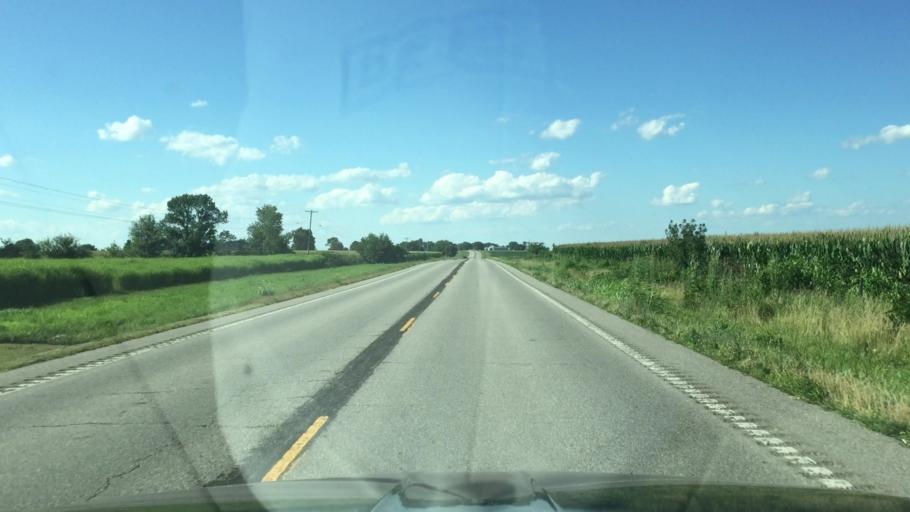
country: US
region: Missouri
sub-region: Moniteau County
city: Tipton
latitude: 38.5947
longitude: -92.7892
